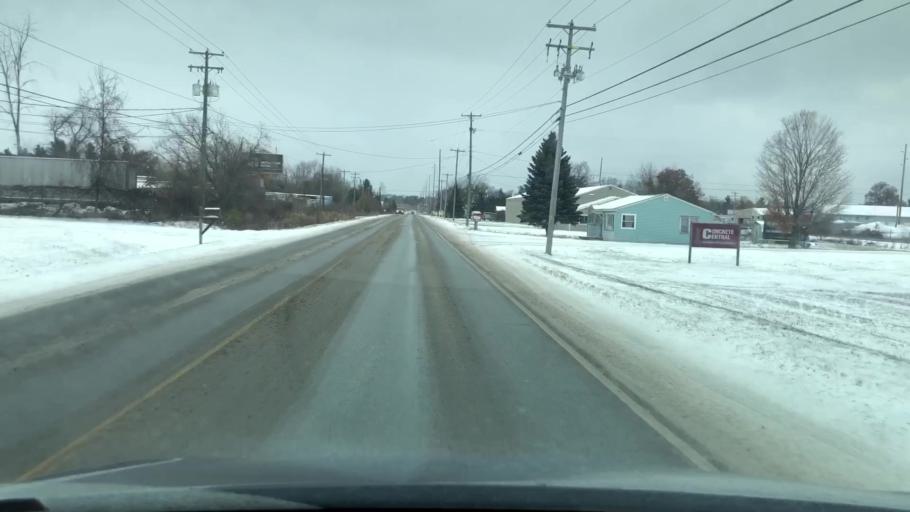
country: US
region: Michigan
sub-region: Grand Traverse County
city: Traverse City
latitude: 44.7174
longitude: -85.6258
